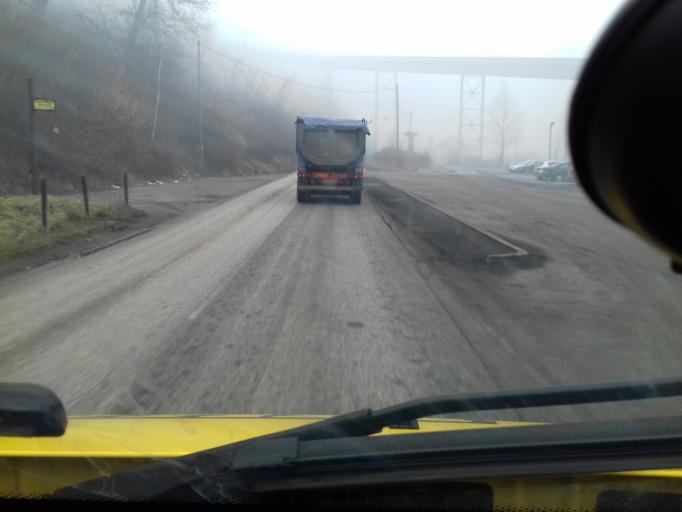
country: BA
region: Federation of Bosnia and Herzegovina
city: Kakanj
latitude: 44.1054
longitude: 18.1157
